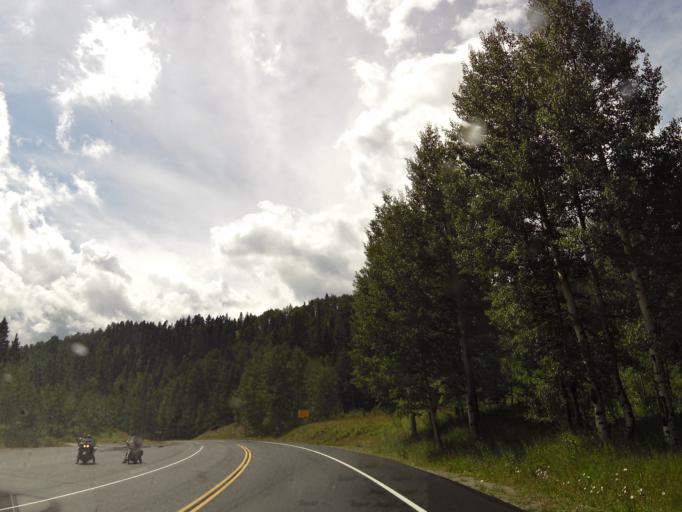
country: US
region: Colorado
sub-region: San Juan County
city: Silverton
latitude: 37.6733
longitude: -107.7939
